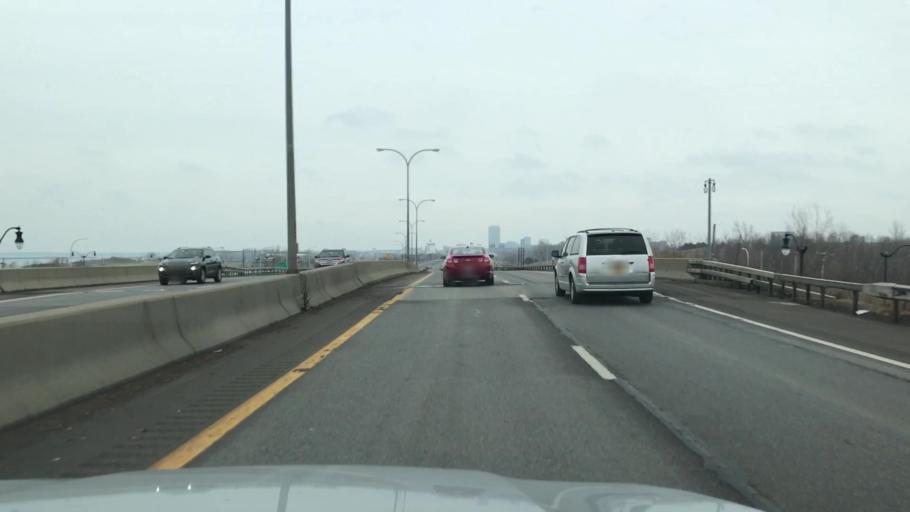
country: US
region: New York
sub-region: Erie County
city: Lackawanna
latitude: 42.8390
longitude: -78.8566
